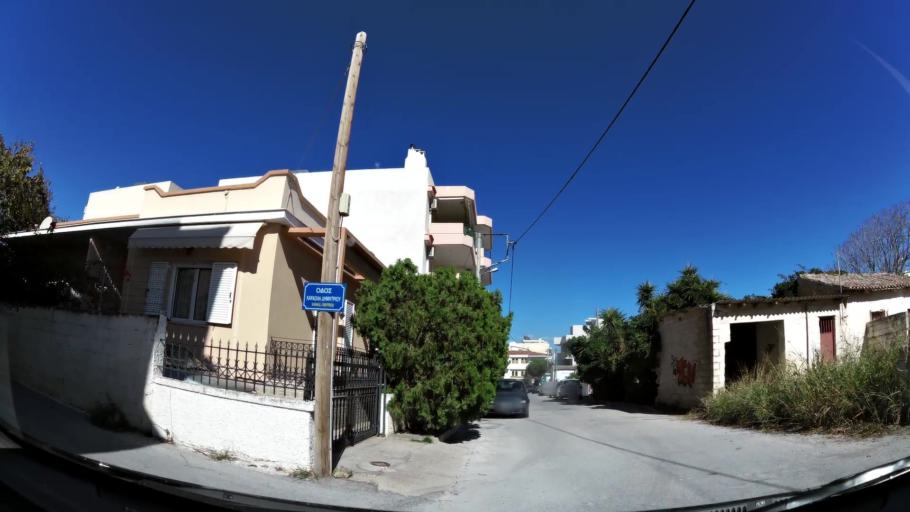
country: GR
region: Attica
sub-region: Nomarchia Anatolikis Attikis
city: Markopoulo
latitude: 37.8850
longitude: 23.9355
